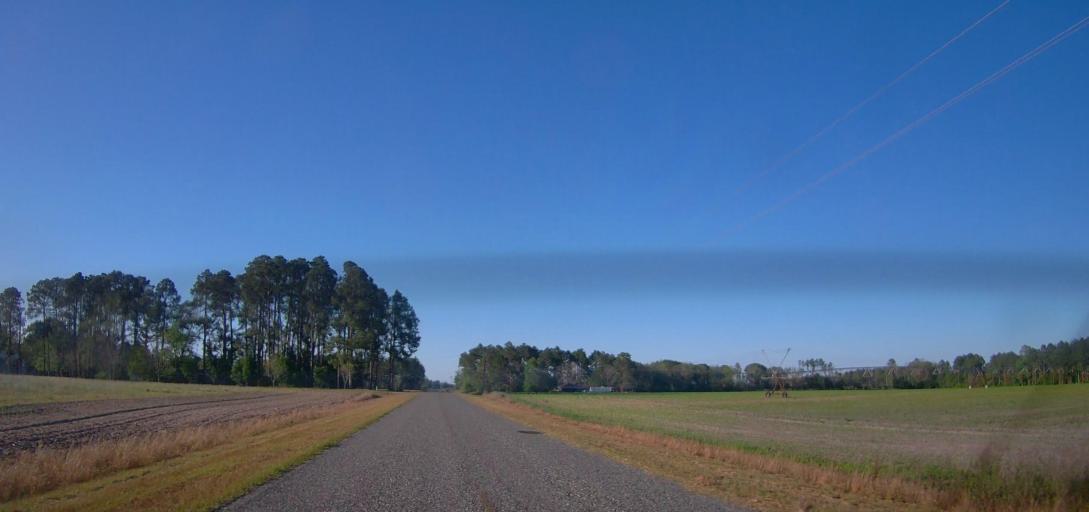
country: US
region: Georgia
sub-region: Ben Hill County
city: Fitzgerald
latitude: 31.6673
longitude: -83.1468
